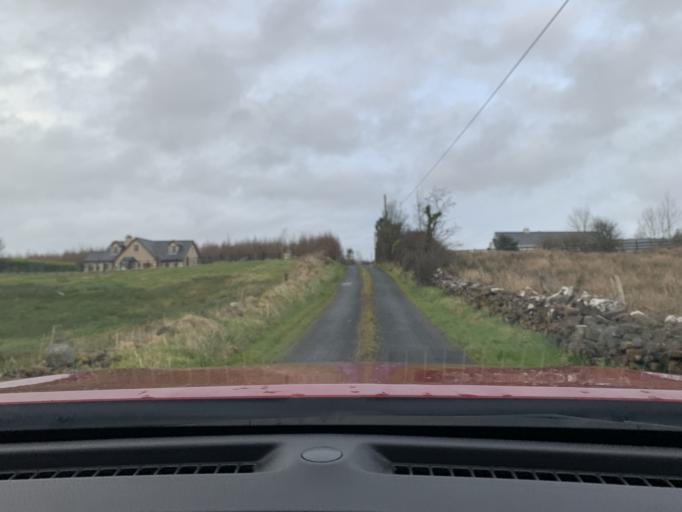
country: IE
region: Connaught
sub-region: Roscommon
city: Boyle
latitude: 53.9830
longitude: -8.4229
